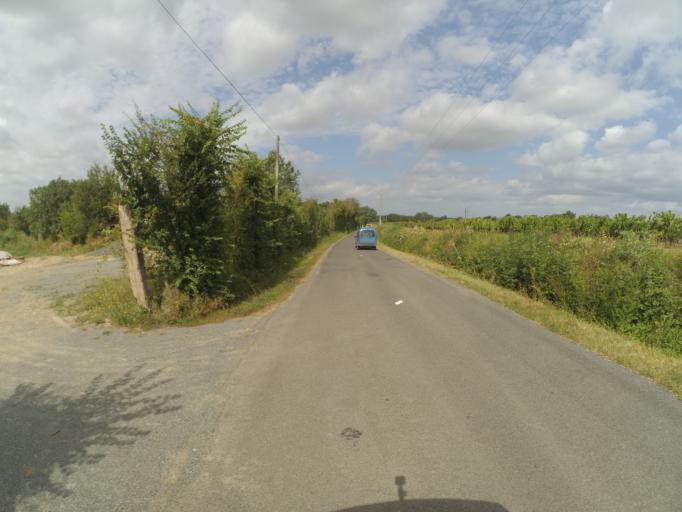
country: FR
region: Pays de la Loire
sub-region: Departement de Maine-et-Loire
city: Saint-Jean
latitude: 47.1929
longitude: -0.3668
